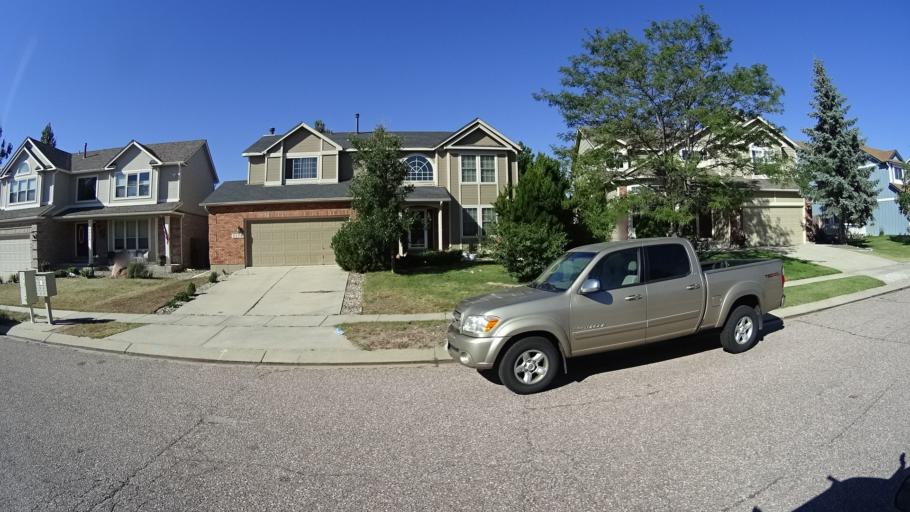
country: US
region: Colorado
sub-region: El Paso County
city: Black Forest
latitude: 38.9605
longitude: -104.7565
